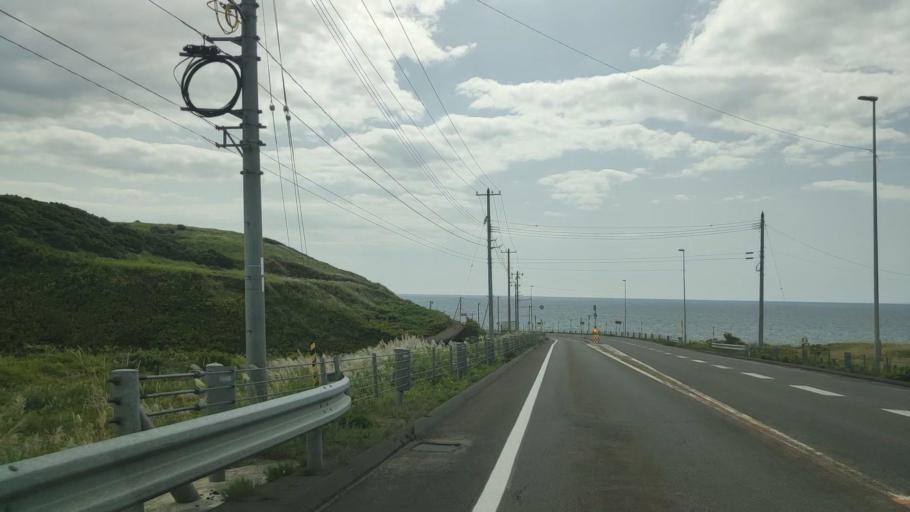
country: JP
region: Hokkaido
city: Rumoi
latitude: 44.5473
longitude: 141.7682
